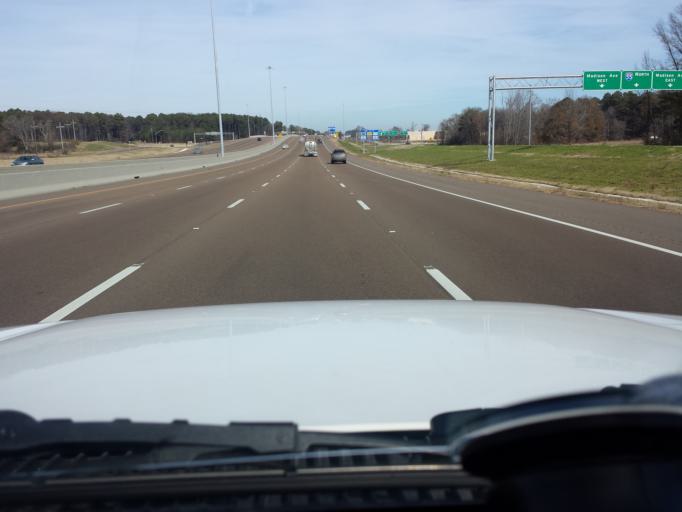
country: US
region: Mississippi
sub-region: Madison County
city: Ridgeland
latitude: 32.4534
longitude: -90.1438
